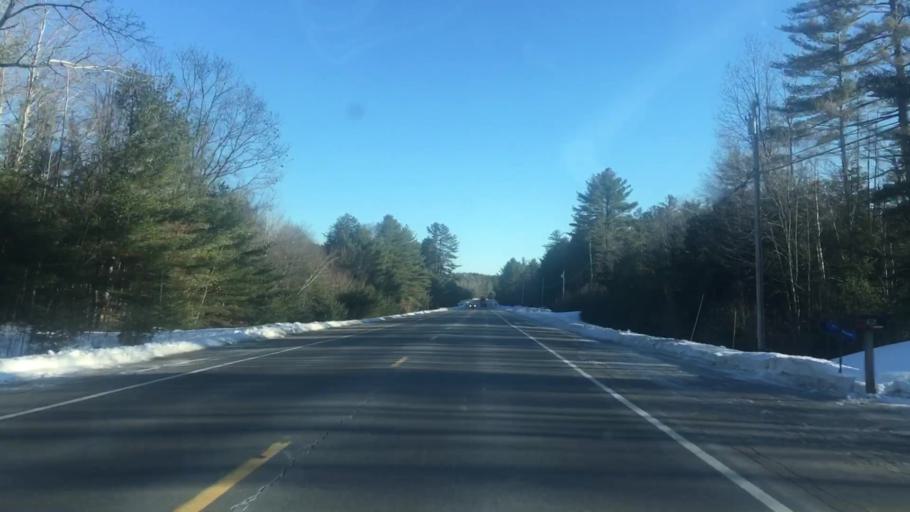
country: US
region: Maine
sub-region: Somerset County
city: Norridgewock
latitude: 44.6900
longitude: -69.7401
